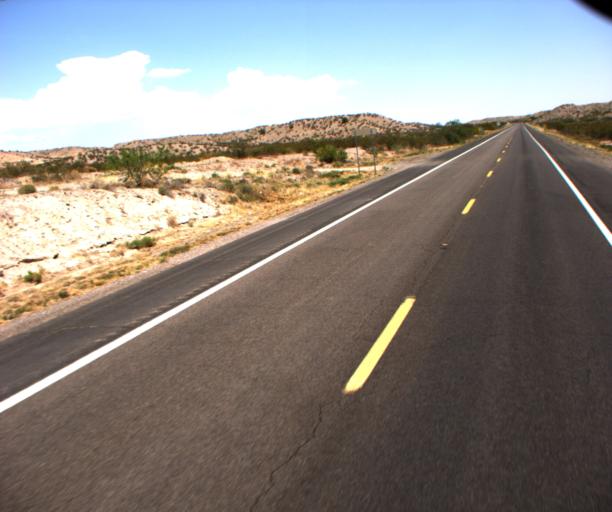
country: US
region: New Mexico
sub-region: Hidalgo County
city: Lordsburg
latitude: 32.6511
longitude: -109.0548
